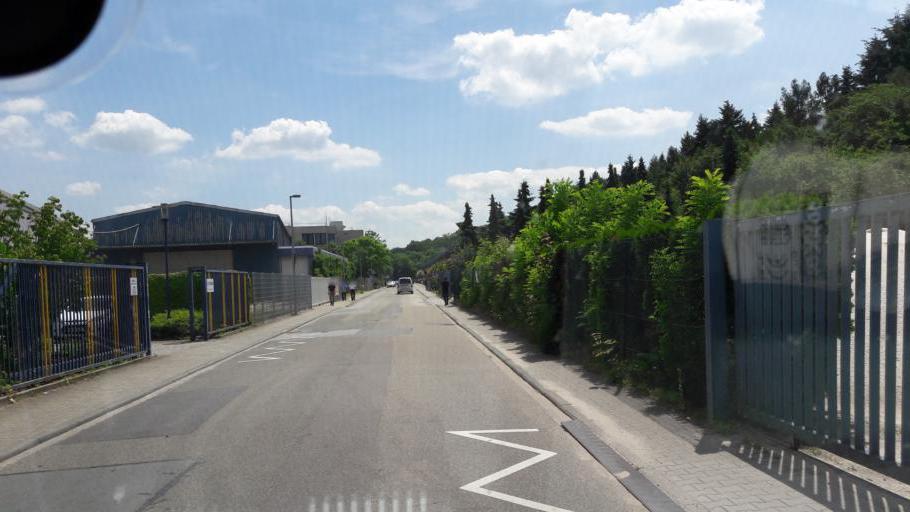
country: DE
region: Baden-Wuerttemberg
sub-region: Karlsruhe Region
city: Walldorf
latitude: 49.2890
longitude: 8.6428
